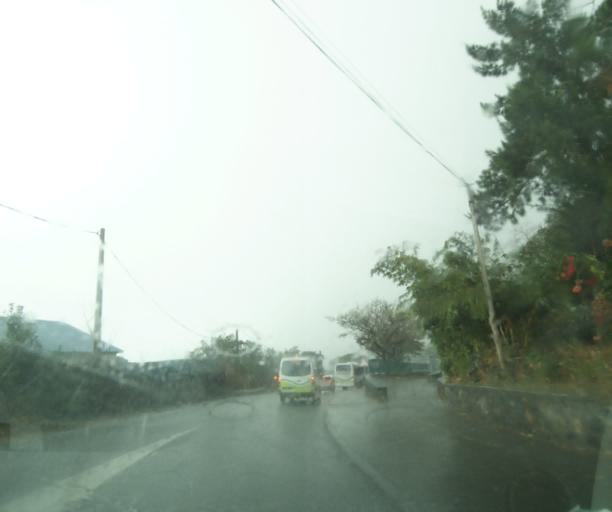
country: RE
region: Reunion
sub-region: Reunion
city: La Possession
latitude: -20.9904
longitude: 55.3301
